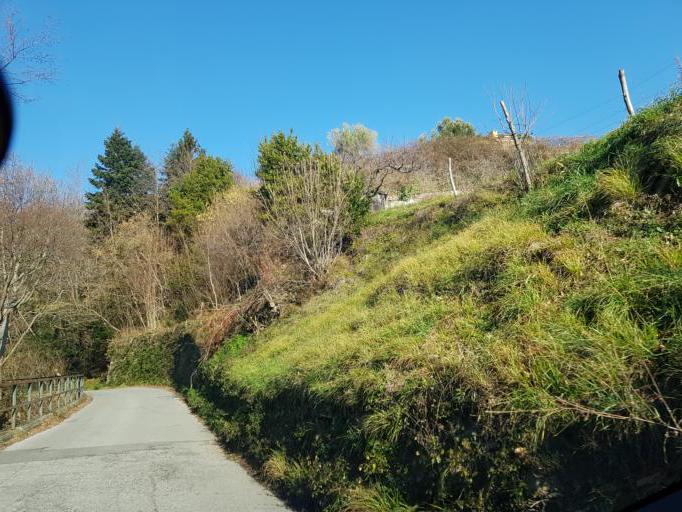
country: IT
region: Liguria
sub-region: Provincia di Genova
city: Campomorone
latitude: 44.5001
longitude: 8.8787
